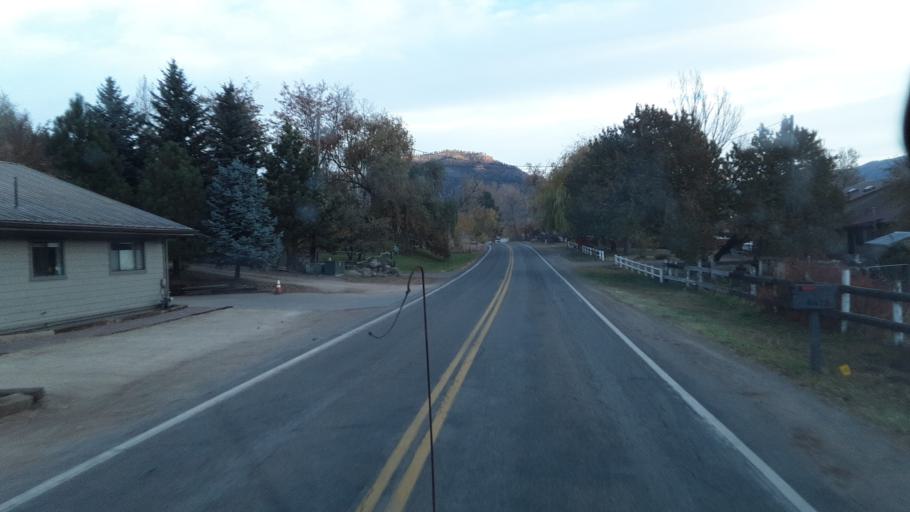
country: US
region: Colorado
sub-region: La Plata County
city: Durango
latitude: 37.3917
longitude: -107.8481
